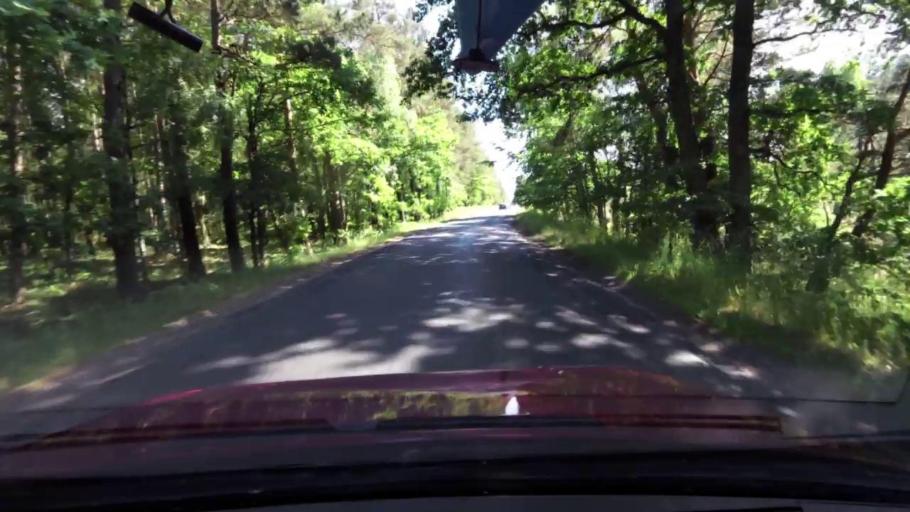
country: PL
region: Pomeranian Voivodeship
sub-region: Powiat slupski
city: Kepice
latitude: 54.3093
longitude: 16.9625
